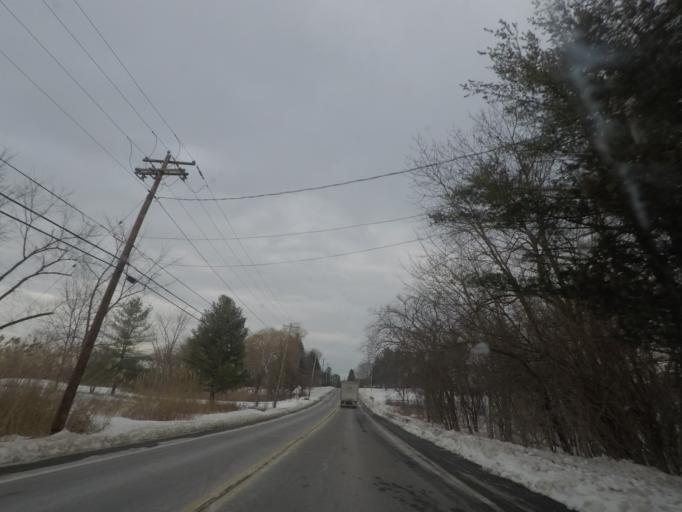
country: US
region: New York
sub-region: Columbia County
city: Stottville
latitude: 42.3314
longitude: -73.7538
